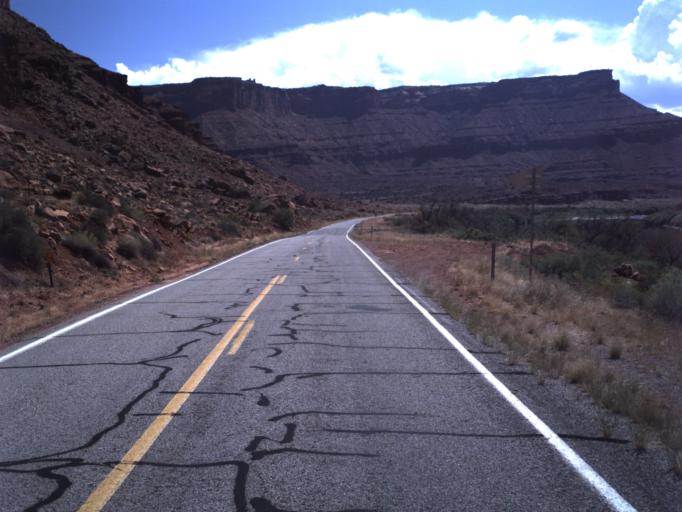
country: US
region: Utah
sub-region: Grand County
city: Moab
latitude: 38.7745
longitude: -109.3268
